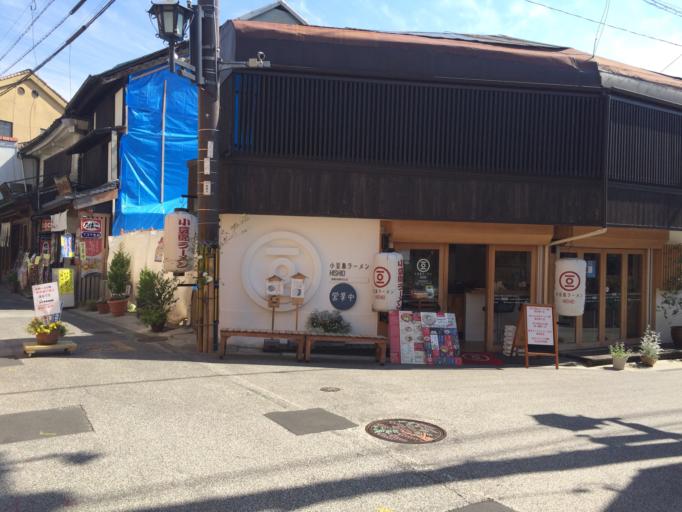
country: JP
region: Okayama
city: Kurashiki
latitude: 34.5979
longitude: 133.7703
